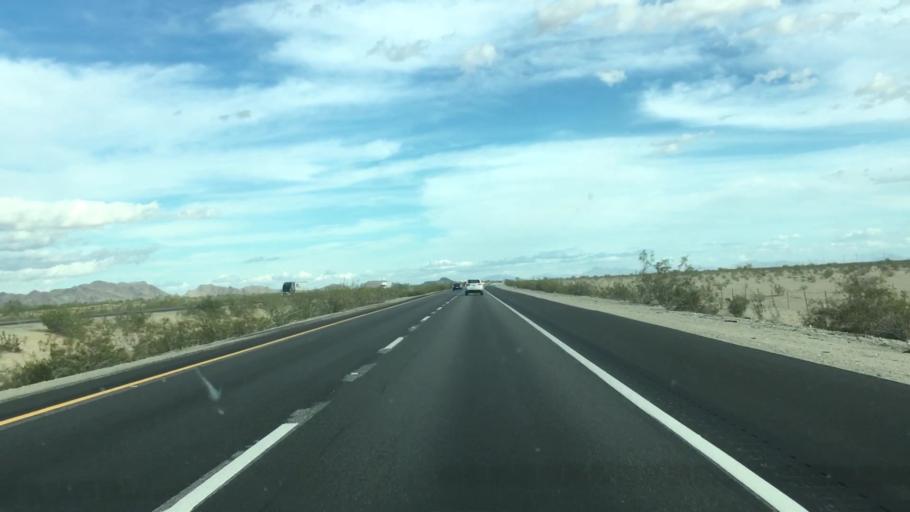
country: US
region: California
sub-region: Riverside County
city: Mesa Verde
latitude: 33.6095
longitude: -114.8442
